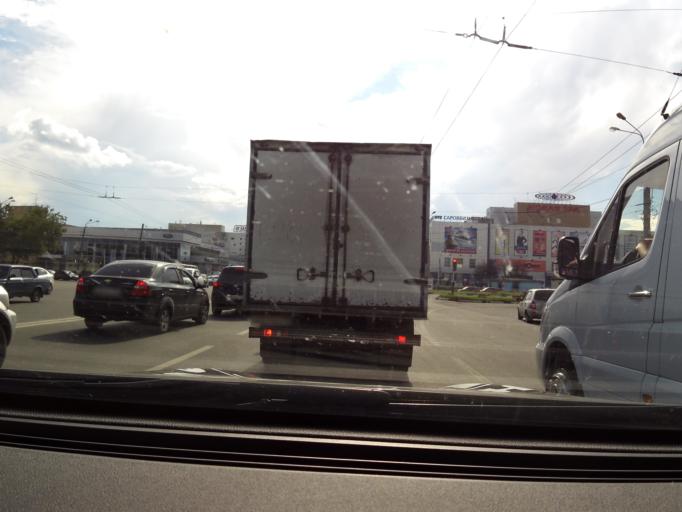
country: RU
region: Nizjnij Novgorod
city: Nizhniy Novgorod
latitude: 56.3198
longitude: 43.9294
